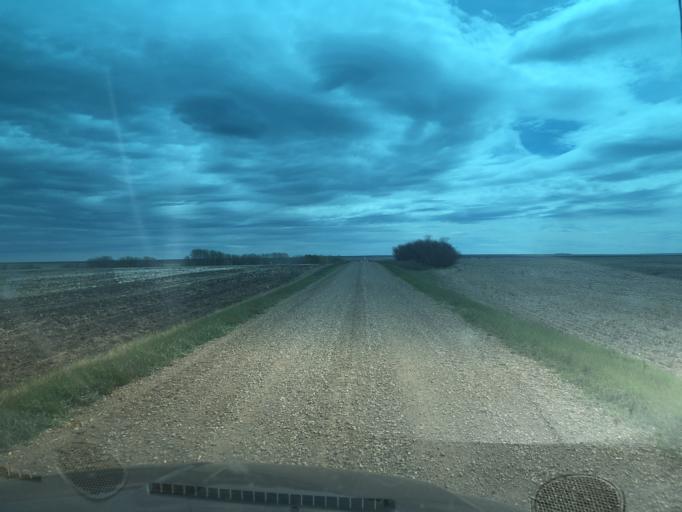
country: CA
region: Alberta
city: Vulcan
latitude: 50.3245
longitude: -113.3569
